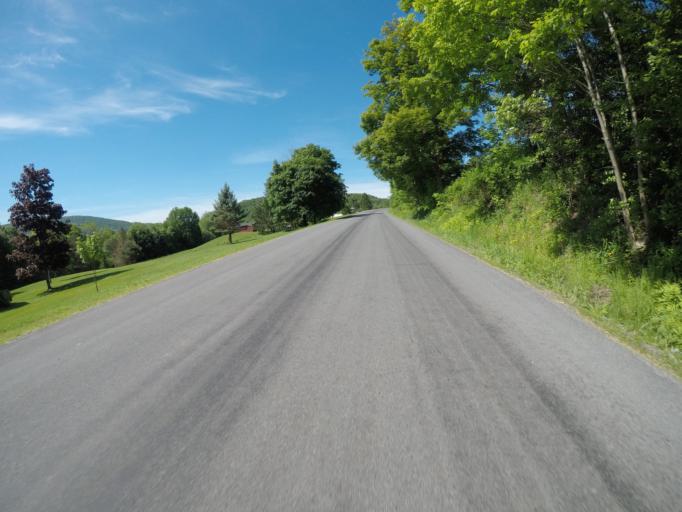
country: US
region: New York
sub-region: Delaware County
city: Delhi
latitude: 42.1856
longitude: -74.7911
